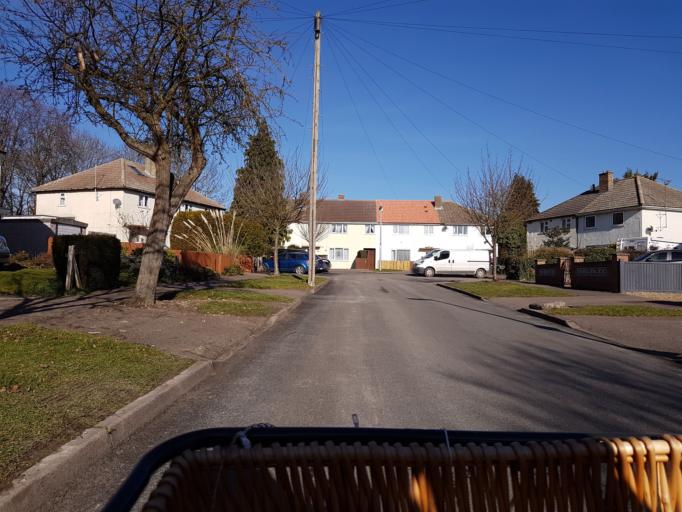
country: GB
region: England
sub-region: Cambridgeshire
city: Fulbourn
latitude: 52.1881
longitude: 0.1793
